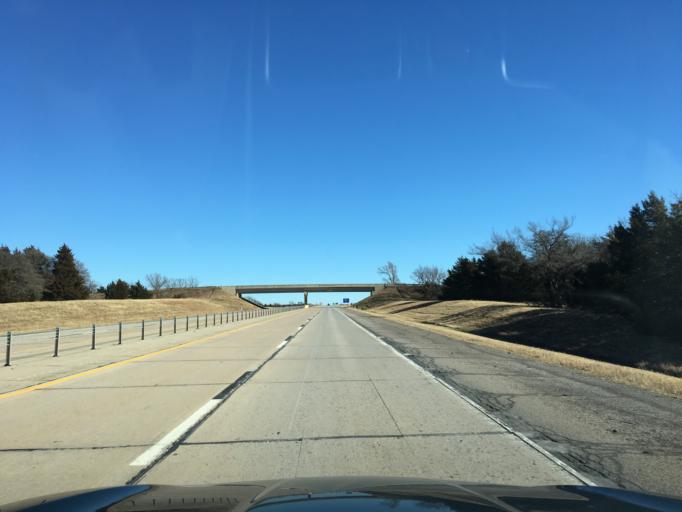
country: US
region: Oklahoma
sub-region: Pawnee County
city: Pawnee
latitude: 36.2247
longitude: -96.8215
